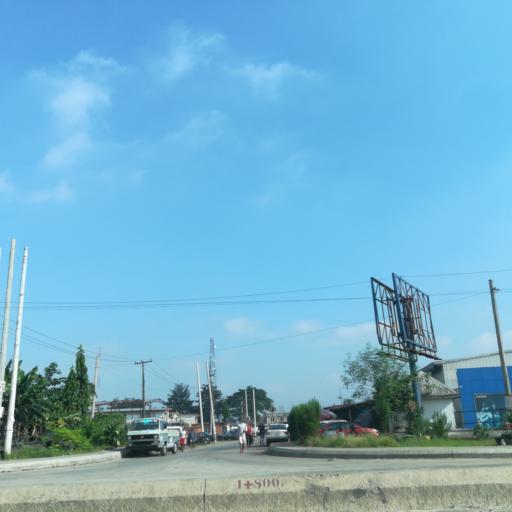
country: NG
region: Rivers
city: Port Harcourt
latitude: 4.8071
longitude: 7.0229
